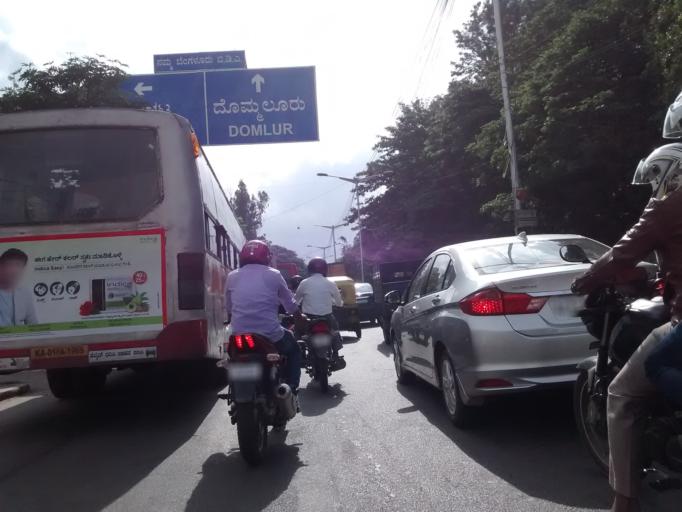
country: IN
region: Karnataka
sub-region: Bangalore Urban
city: Bangalore
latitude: 12.9593
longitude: 77.6554
